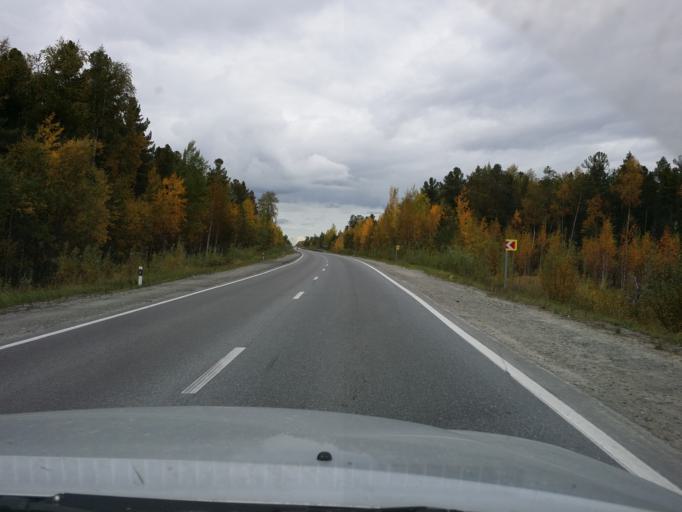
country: RU
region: Khanty-Mansiyskiy Avtonomnyy Okrug
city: Langepas
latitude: 61.2251
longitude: 75.3276
